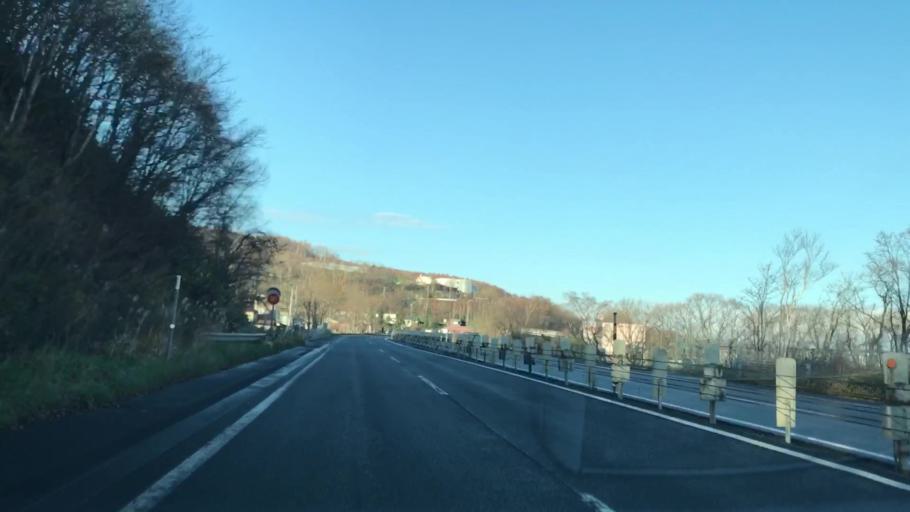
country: JP
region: Hokkaido
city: Otaru
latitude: 43.1405
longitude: 141.1496
